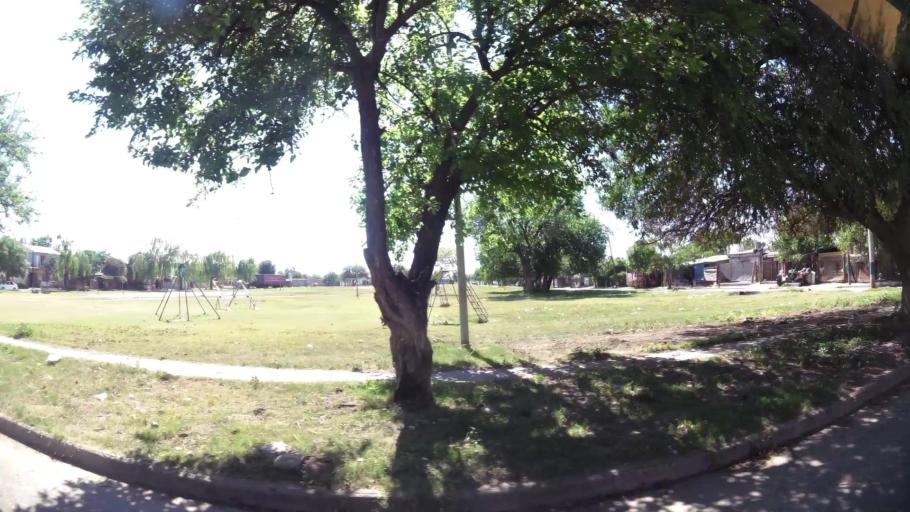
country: AR
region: Cordoba
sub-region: Departamento de Capital
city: Cordoba
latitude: -31.4423
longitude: -64.1305
